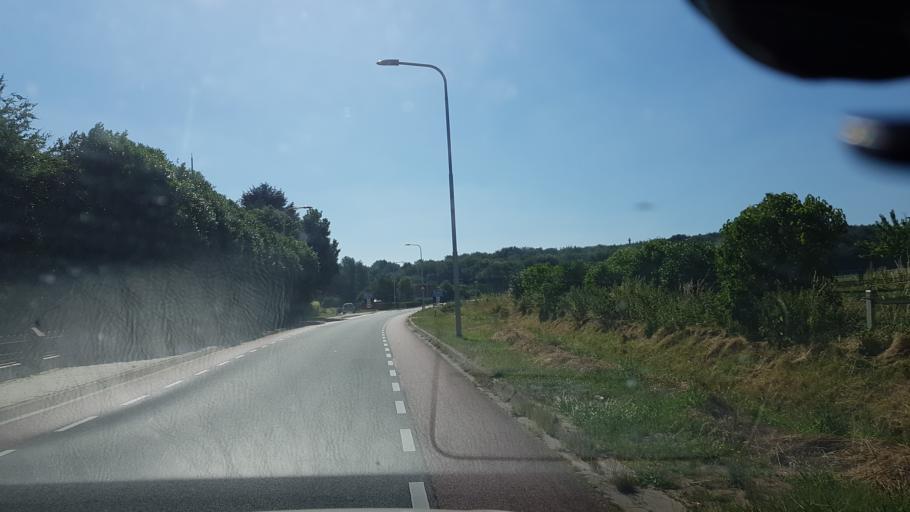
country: NL
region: Gelderland
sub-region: Gemeente Groesbeek
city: Bredeweg
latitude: 51.7499
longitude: 5.9494
